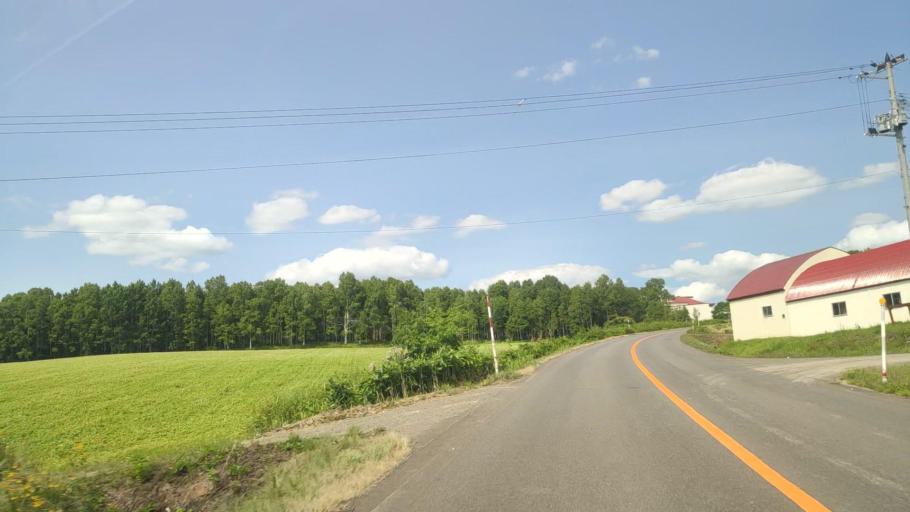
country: JP
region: Hokkaido
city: Nayoro
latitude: 44.2796
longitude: 142.4235
